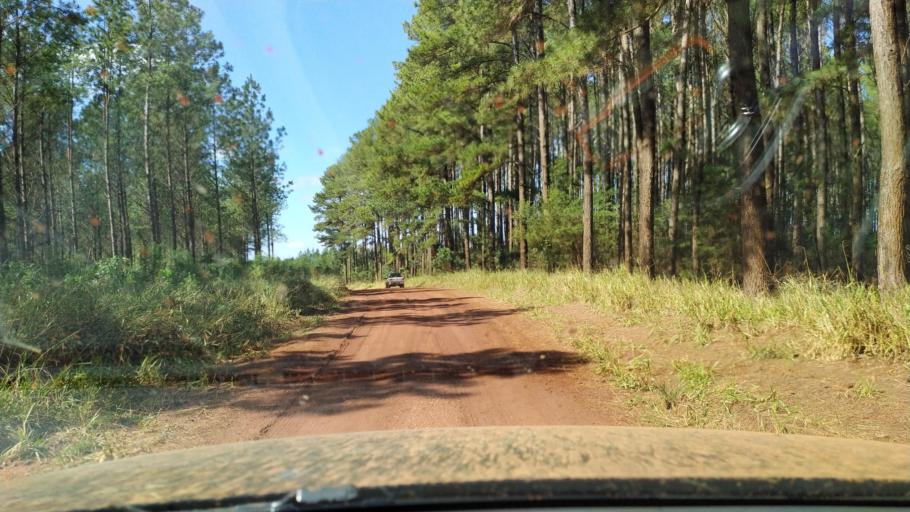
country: AR
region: Corrientes
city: Santo Tome
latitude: -28.4012
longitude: -56.0162
